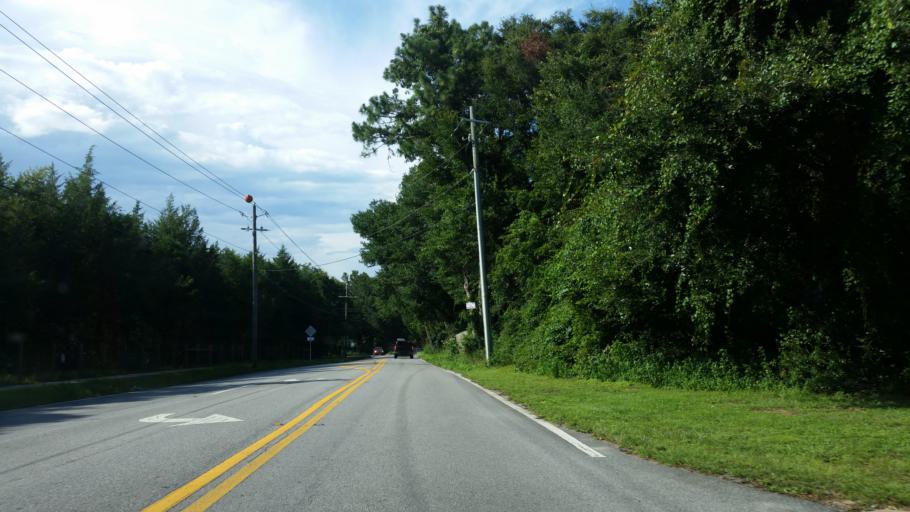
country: US
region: Florida
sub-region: Santa Rosa County
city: Pace
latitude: 30.6310
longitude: -87.1312
